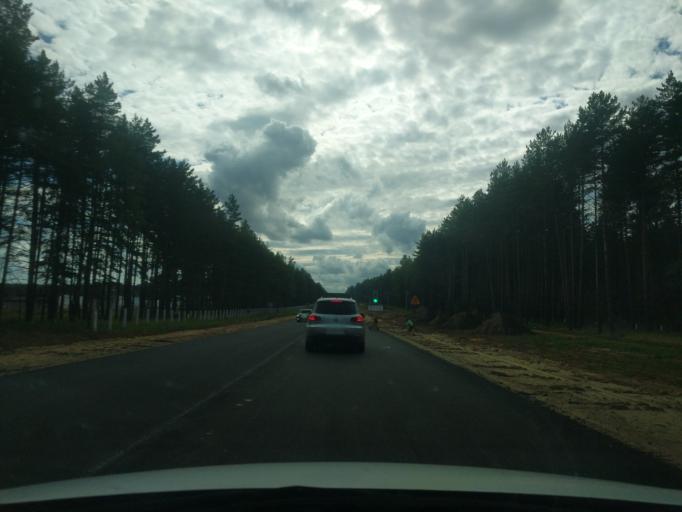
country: RU
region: Jaroslavl
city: Levashevo
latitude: 57.6808
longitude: 40.5959
